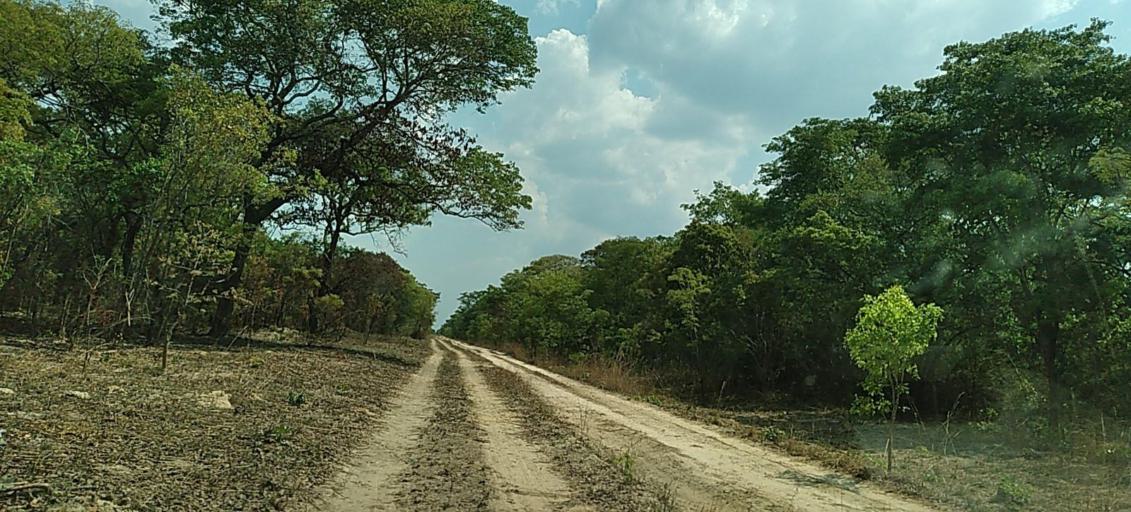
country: ZM
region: Copperbelt
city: Mpongwe
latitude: -13.8215
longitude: 27.9437
